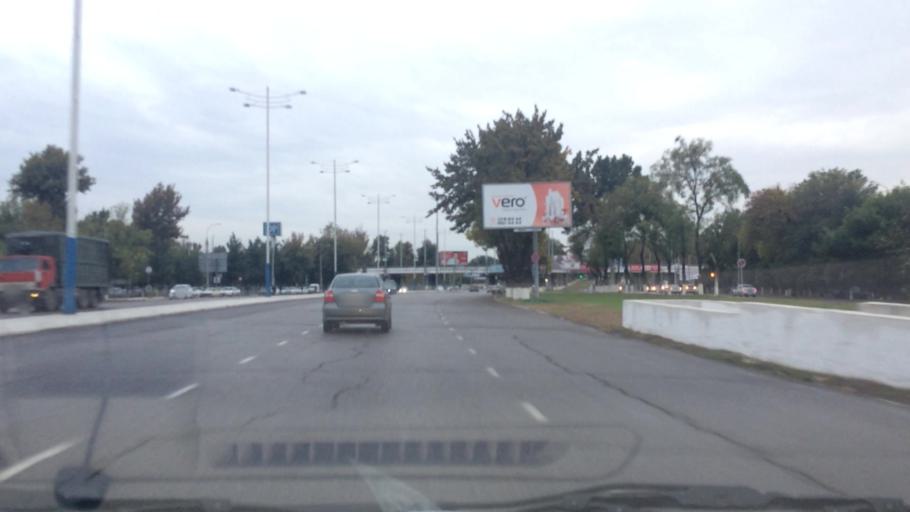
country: UZ
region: Toshkent Shahri
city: Tashkent
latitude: 41.2579
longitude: 69.1949
